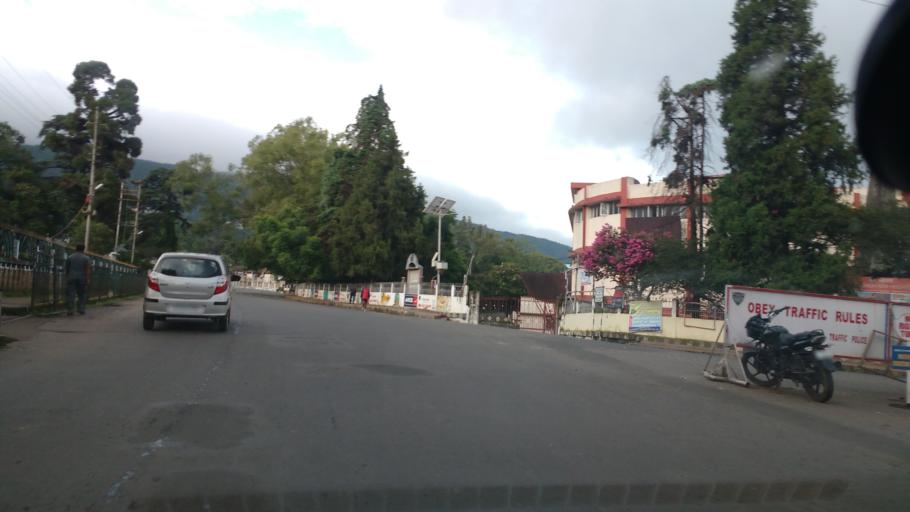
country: IN
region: Meghalaya
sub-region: East Khasi Hills
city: Shillong
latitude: 25.5700
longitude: 91.8843
